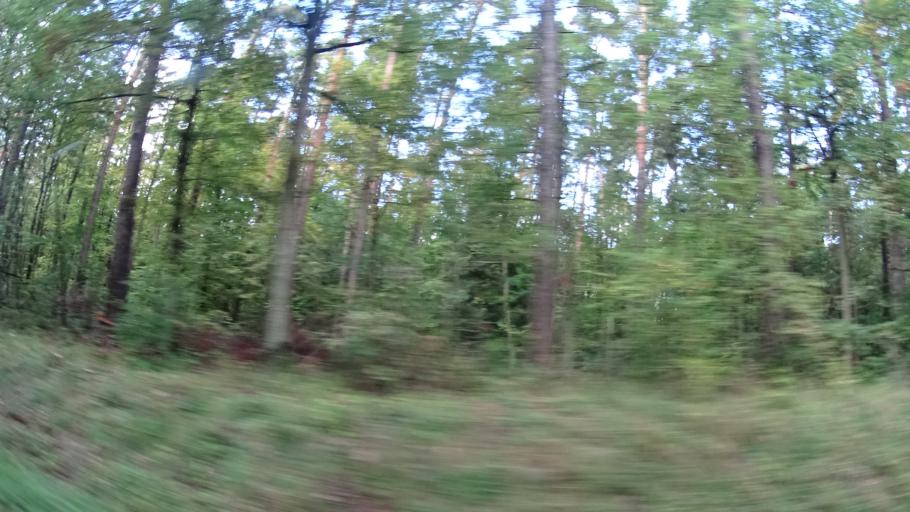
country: DE
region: Bavaria
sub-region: Regierungsbezirk Unterfranken
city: Volkach
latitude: 49.8624
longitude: 10.2649
